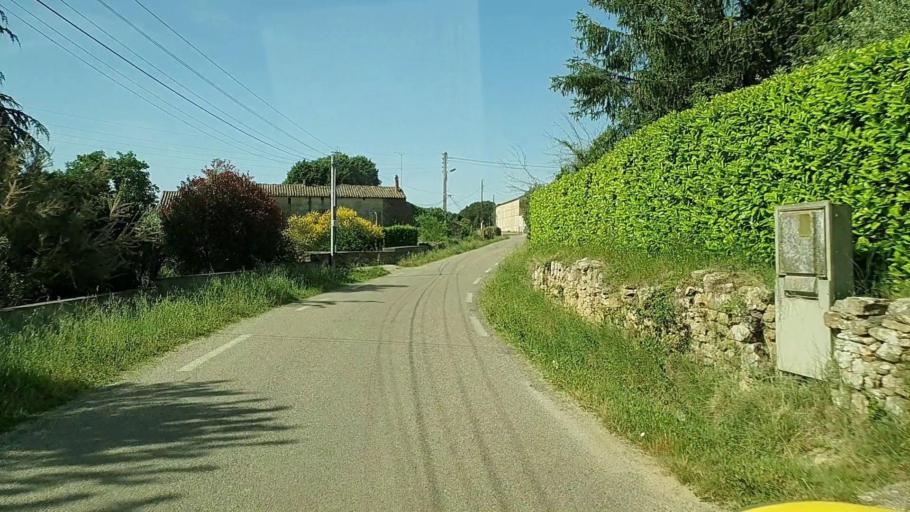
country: FR
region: Languedoc-Roussillon
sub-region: Departement du Gard
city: Sabran
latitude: 44.1450
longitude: 4.4947
